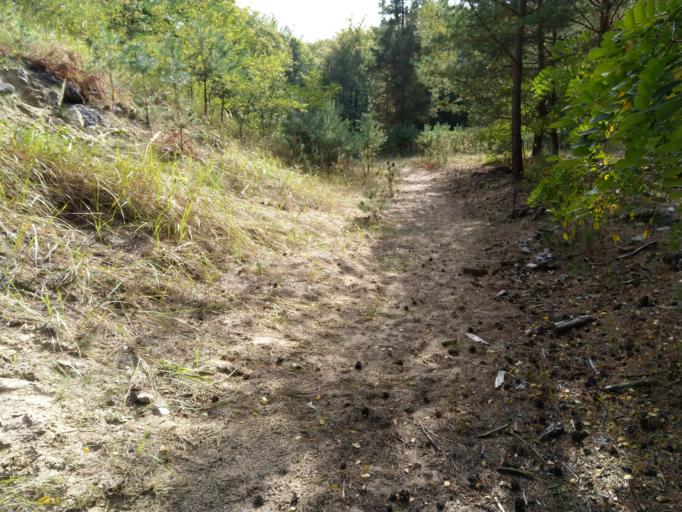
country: DE
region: Brandenburg
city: Erkner
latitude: 52.4446
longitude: 13.7331
